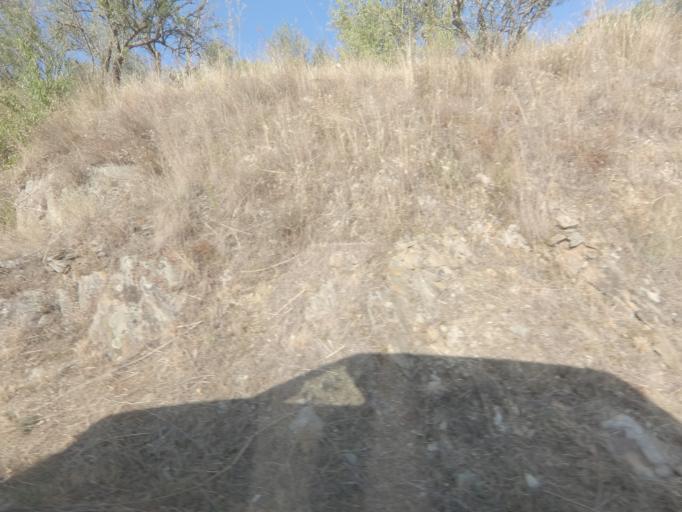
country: PT
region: Vila Real
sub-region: Sabrosa
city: Sabrosa
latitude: 41.2395
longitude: -7.5217
